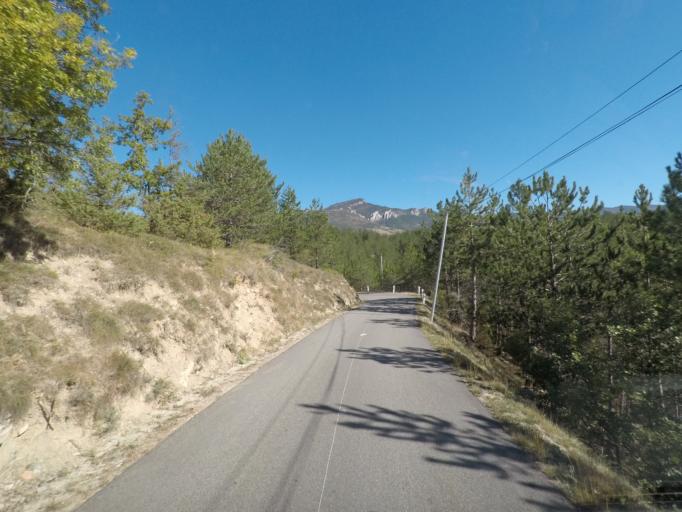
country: FR
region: Rhone-Alpes
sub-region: Departement de la Drome
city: Die
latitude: 44.6206
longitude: 5.2961
